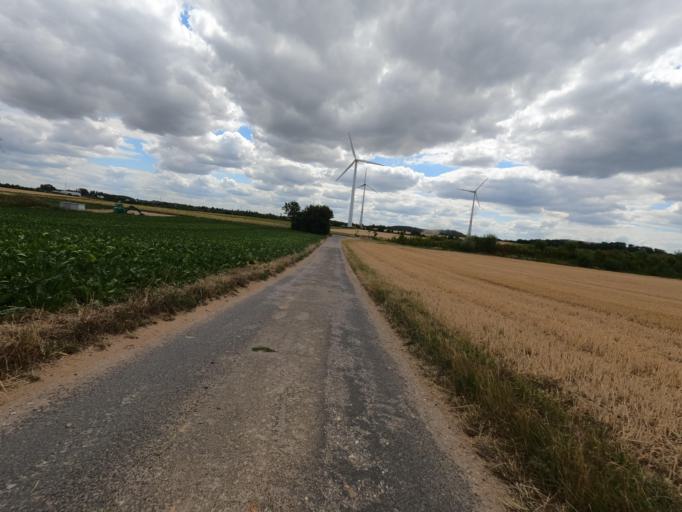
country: DE
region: North Rhine-Westphalia
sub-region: Regierungsbezirk Koln
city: Alsdorf
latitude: 50.8970
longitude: 6.1594
